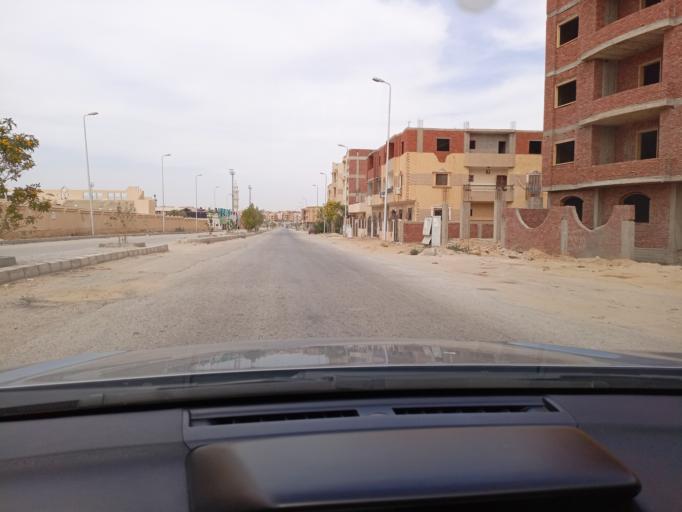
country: EG
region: Muhafazat al Qalyubiyah
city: Al Khankah
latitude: 30.2476
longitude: 31.4964
